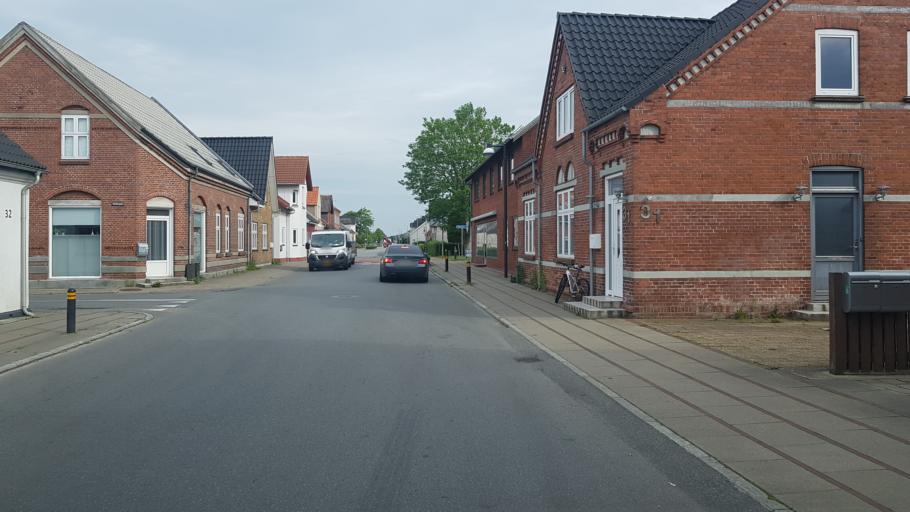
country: DK
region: South Denmark
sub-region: Esbjerg Kommune
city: Bramming
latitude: 55.4713
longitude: 8.8011
